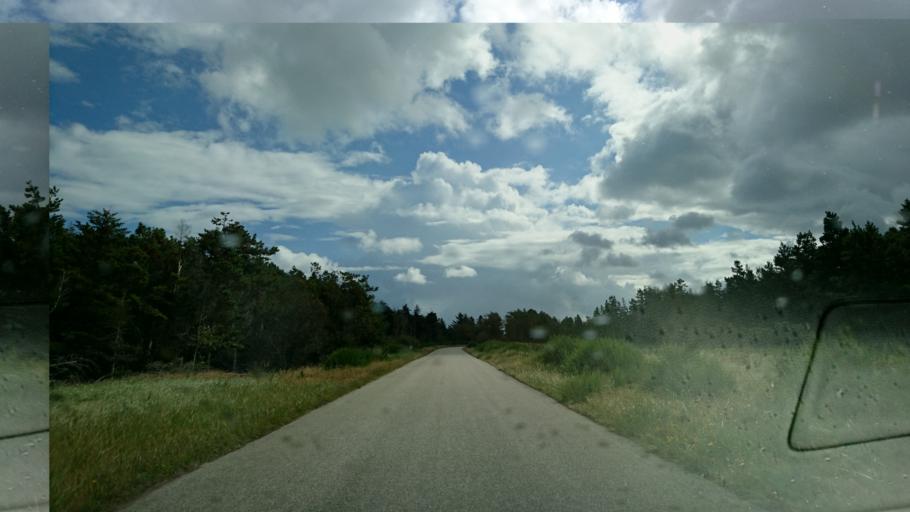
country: DK
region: North Denmark
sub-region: Frederikshavn Kommune
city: Skagen
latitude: 57.7201
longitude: 10.5217
